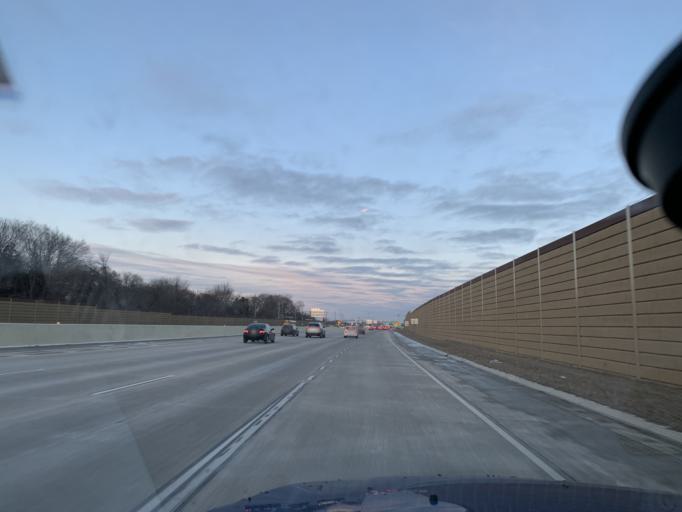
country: US
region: Wisconsin
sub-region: Dane County
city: Shorewood Hills
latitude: 43.0277
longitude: -89.4647
